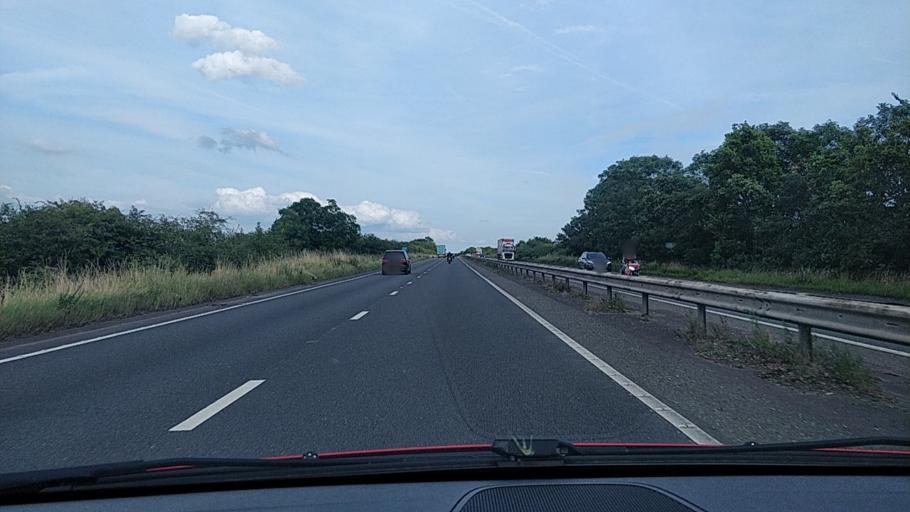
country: GB
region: Wales
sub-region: Wrexham
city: Rossett
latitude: 53.1581
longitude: -2.9386
